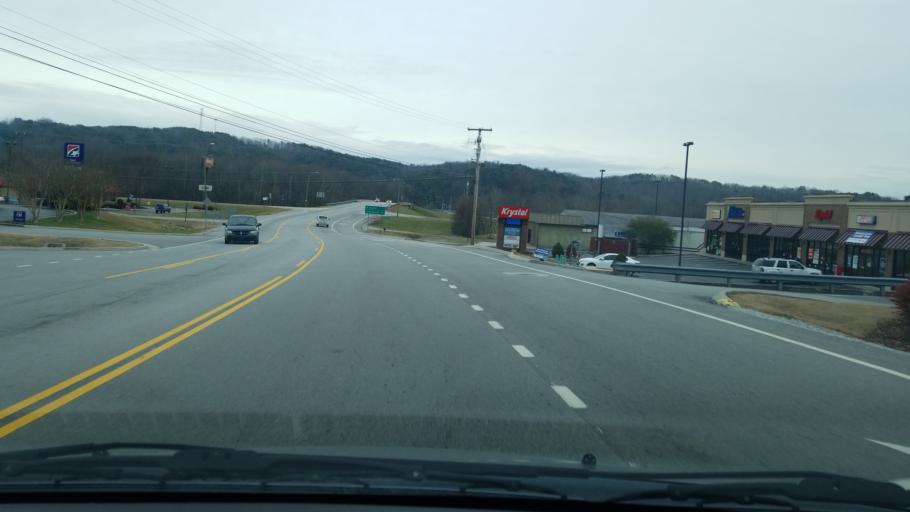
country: US
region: Tennessee
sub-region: Hamilton County
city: Soddy-Daisy
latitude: 35.2367
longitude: -85.1988
